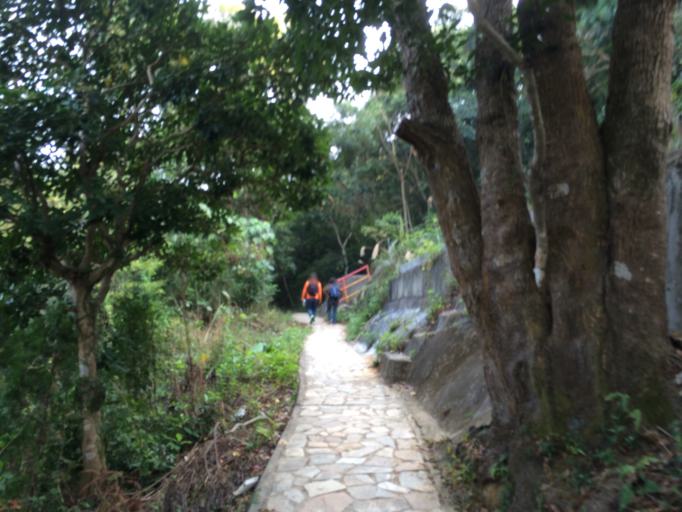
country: HK
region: Tai Po
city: Tai Po
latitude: 22.4521
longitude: 114.2142
